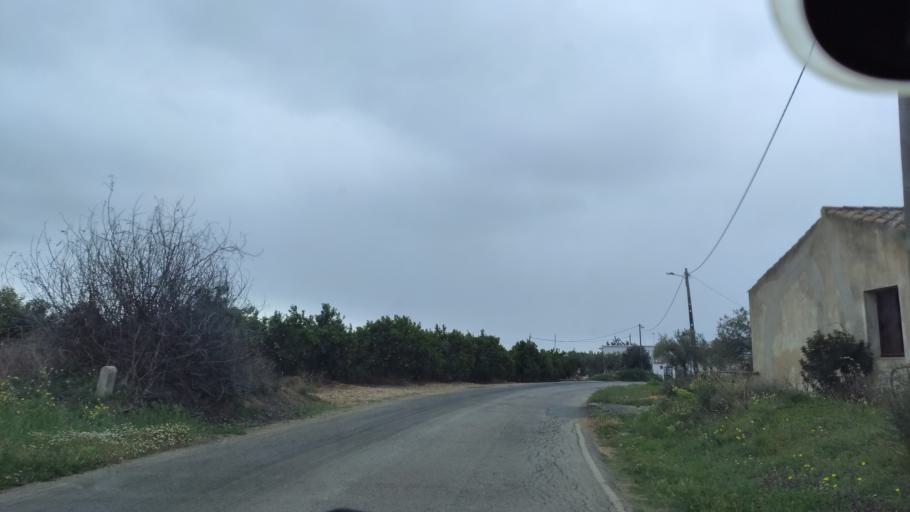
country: PT
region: Faro
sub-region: Faro
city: Santa Barbara de Nexe
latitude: 37.0828
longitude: -7.9230
